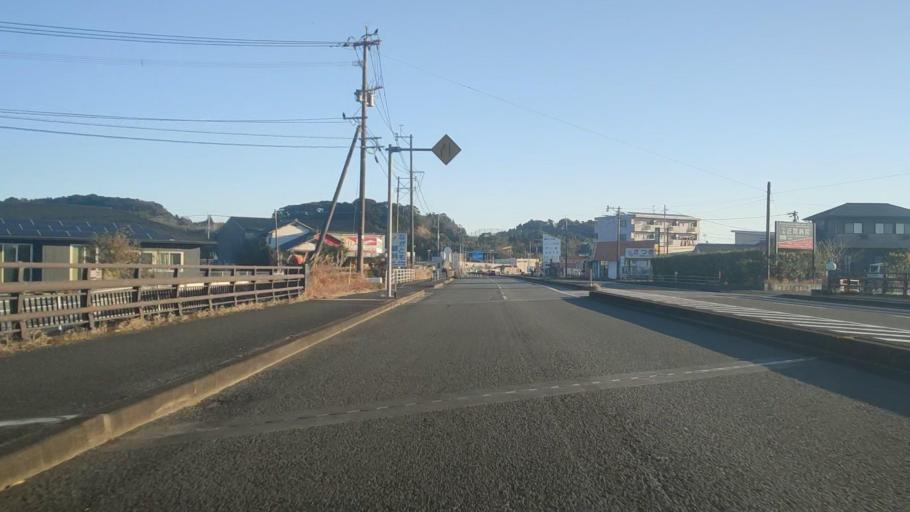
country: JP
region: Miyazaki
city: Takanabe
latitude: 32.0724
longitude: 131.4931
